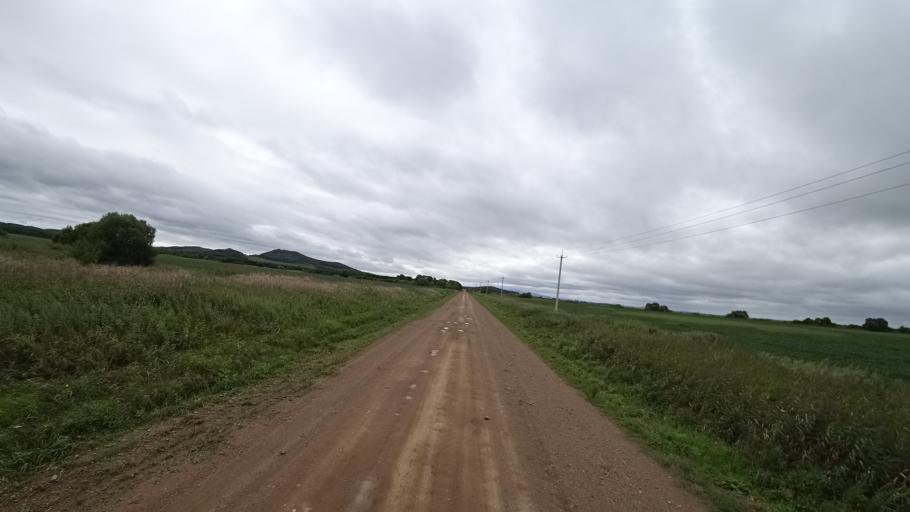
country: RU
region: Primorskiy
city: Chernigovka
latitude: 44.4907
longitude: 132.5721
